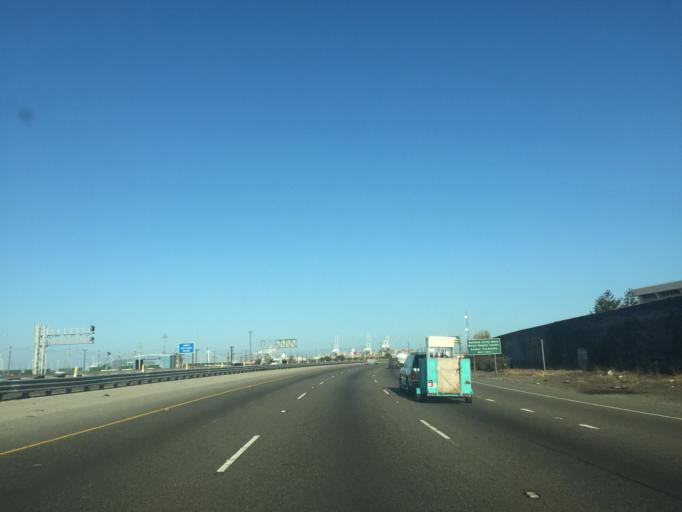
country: US
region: California
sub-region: Alameda County
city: Oakland
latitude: 37.8027
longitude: -122.2998
